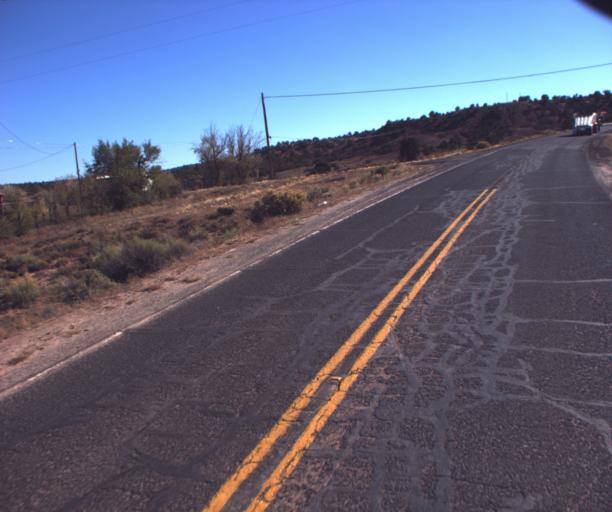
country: US
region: Arizona
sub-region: Apache County
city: Ganado
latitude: 35.7063
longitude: -109.5423
